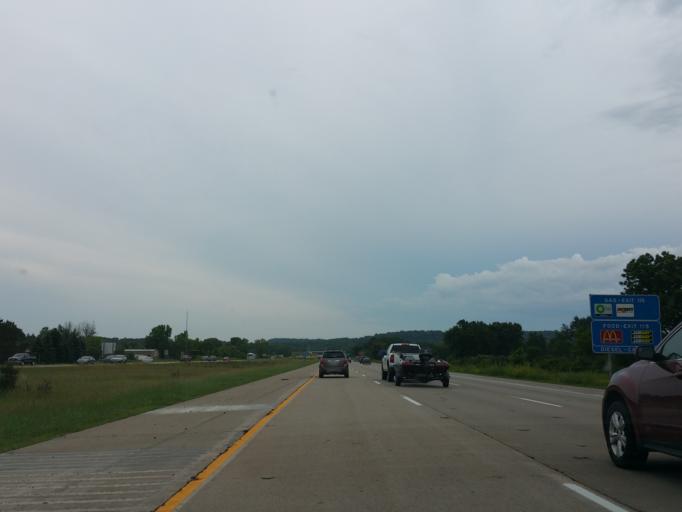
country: US
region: Wisconsin
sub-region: Columbia County
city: Poynette
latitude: 43.4040
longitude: -89.4672
